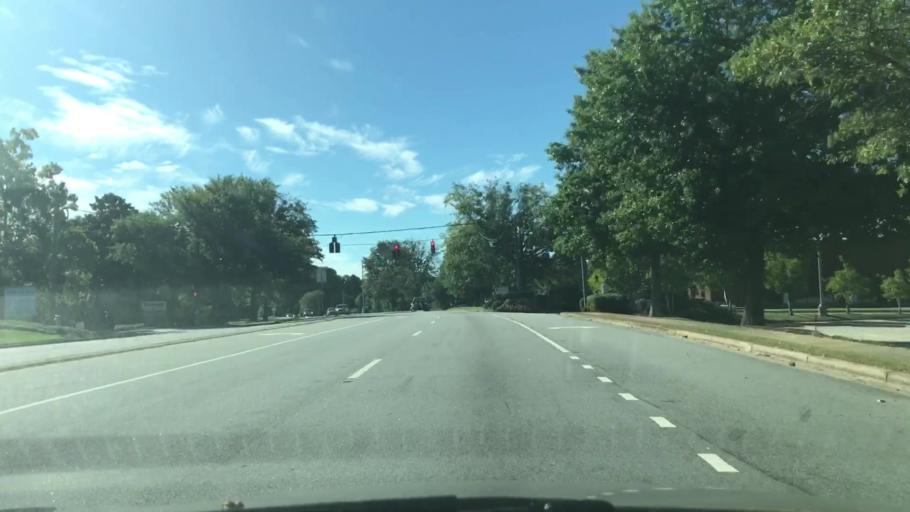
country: US
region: Georgia
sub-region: Gwinnett County
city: Mountain Park
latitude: 33.8191
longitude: -84.1202
